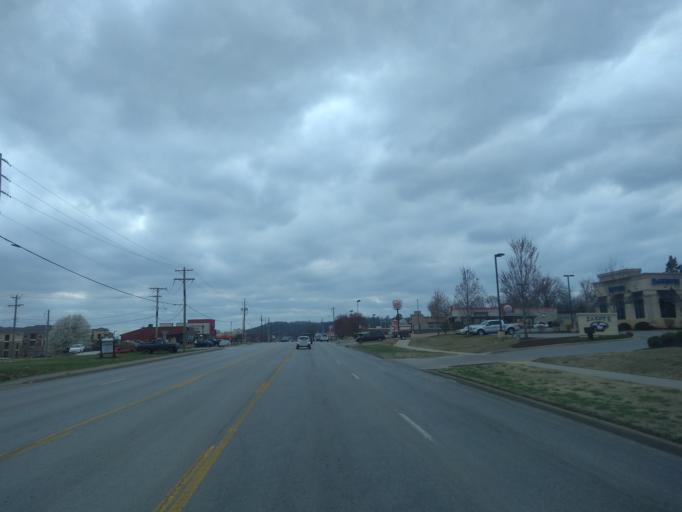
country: US
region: Arkansas
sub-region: Washington County
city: Fayetteville
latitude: 36.0567
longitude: -94.1840
